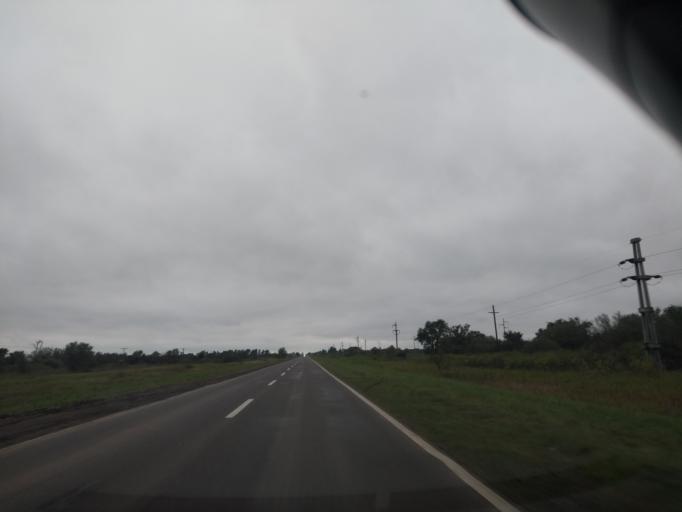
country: AR
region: Chaco
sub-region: Departamento de Quitilipi
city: Quitilipi
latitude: -26.8671
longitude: -60.2642
